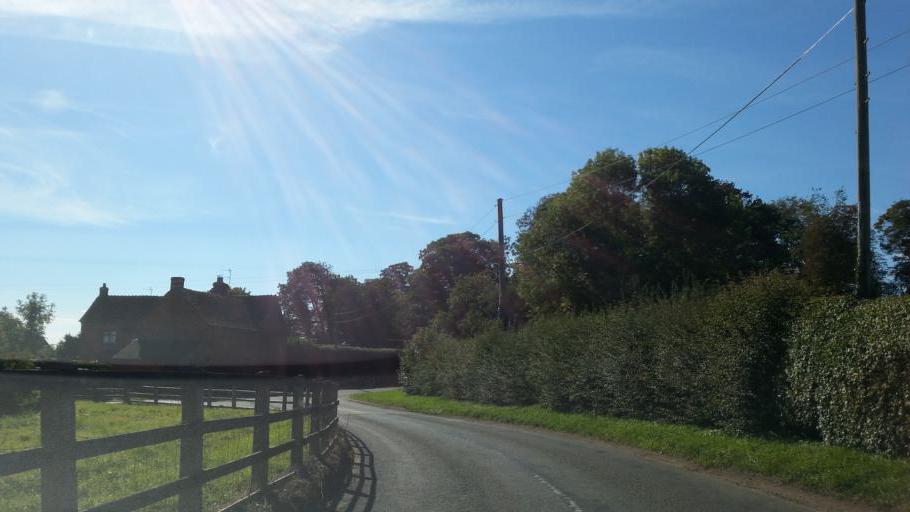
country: GB
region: England
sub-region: Staffordshire
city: Stafford
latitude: 52.8092
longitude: -2.1599
